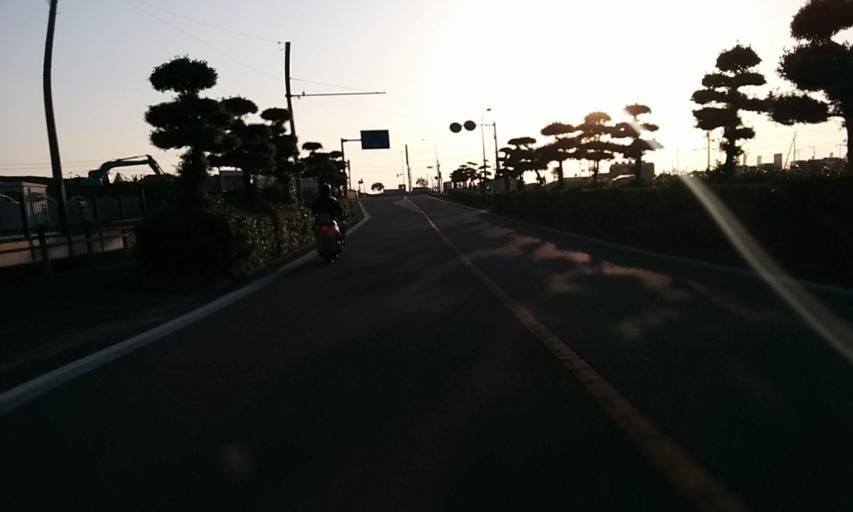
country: JP
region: Ehime
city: Masaki-cho
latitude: 33.7698
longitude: 132.7098
